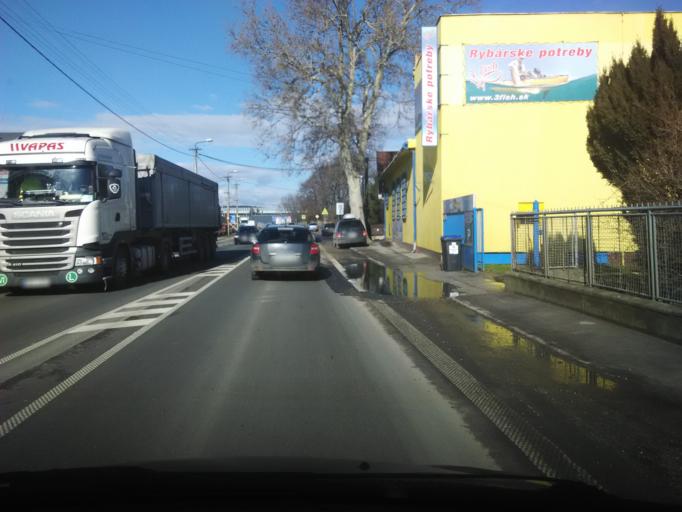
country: SK
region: Nitriansky
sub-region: Okres Nitra
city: Nitra
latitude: 48.2842
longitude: 18.0885
